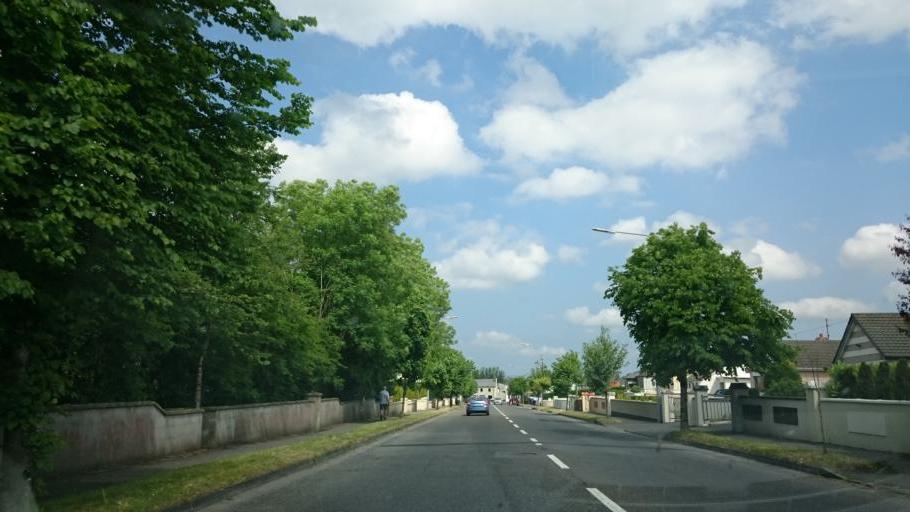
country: IE
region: Connaught
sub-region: Sligo
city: Tobercurry
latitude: 53.9617
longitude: -8.7936
